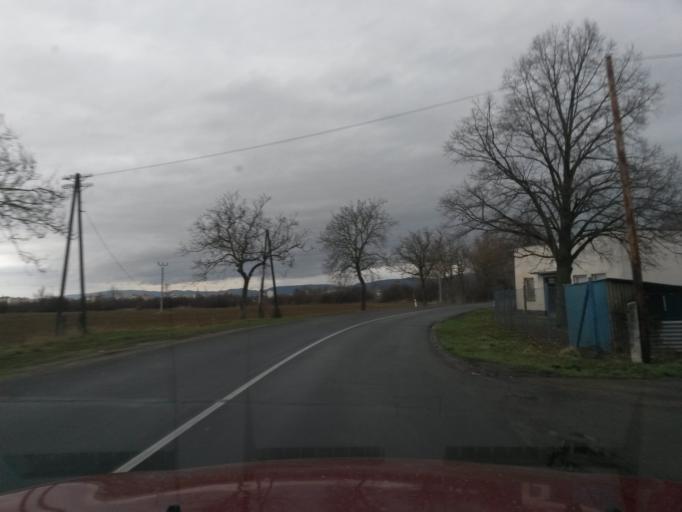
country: SK
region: Kosicky
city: Michalovce
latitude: 48.7323
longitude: 21.9178
